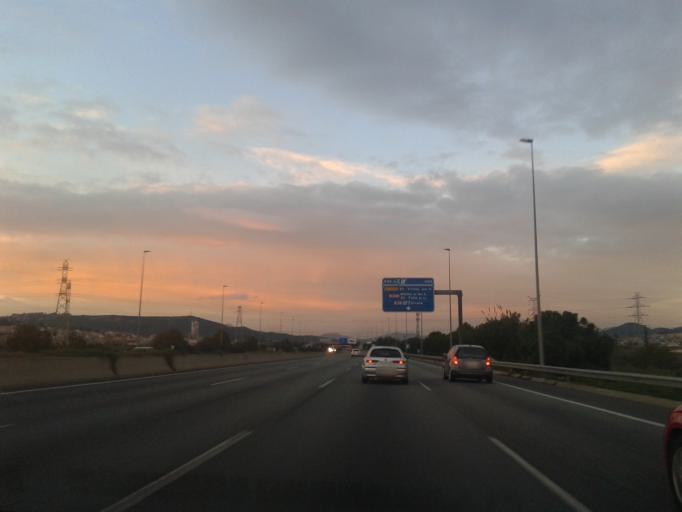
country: ES
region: Catalonia
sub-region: Provincia de Barcelona
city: Santa Coloma de Cervello
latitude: 41.3824
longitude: 2.0236
